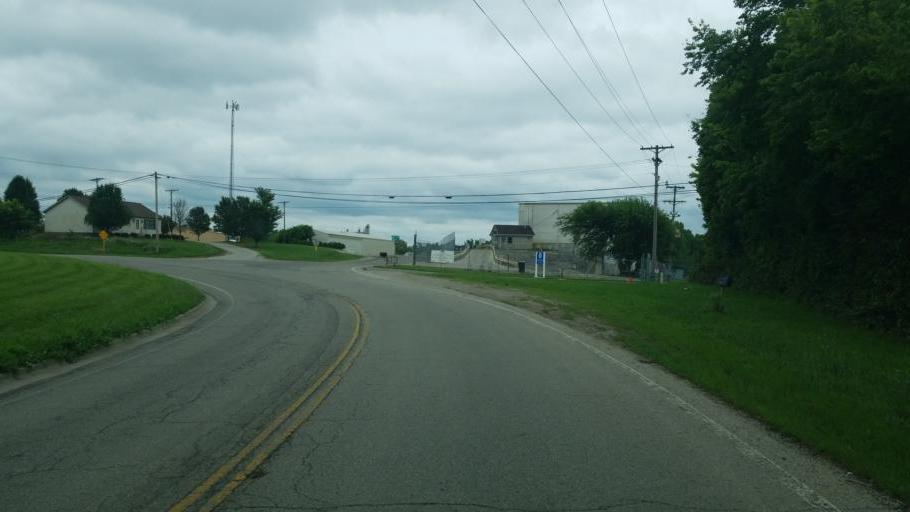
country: US
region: Ohio
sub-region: Pickaway County
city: Circleville
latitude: 39.6111
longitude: -82.9552
